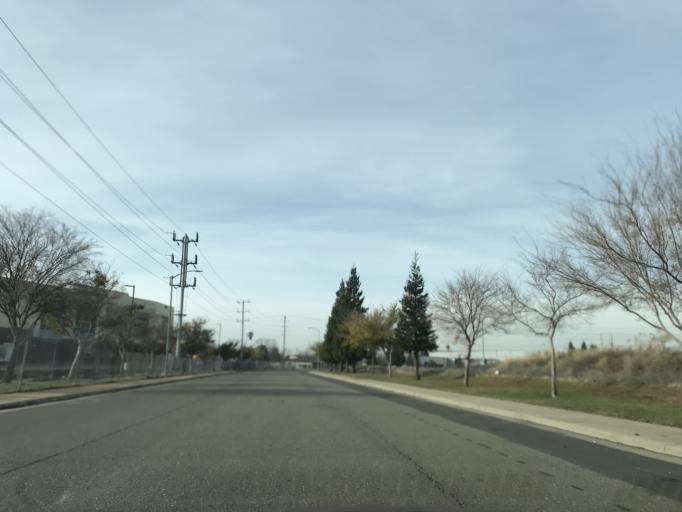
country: US
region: California
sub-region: Sacramento County
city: Arden-Arcade
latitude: 38.6422
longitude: -121.4084
